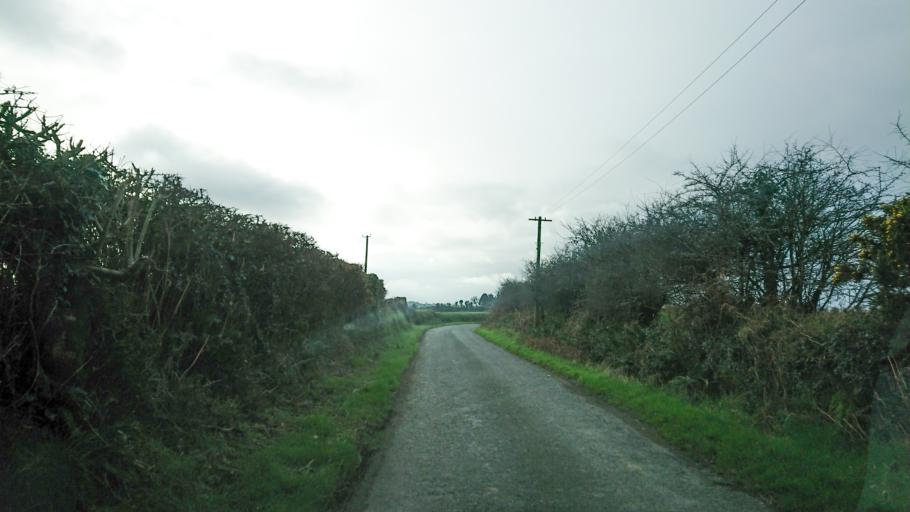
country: IE
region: Munster
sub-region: Waterford
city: Tra Mhor
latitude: 52.1938
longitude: -7.1730
